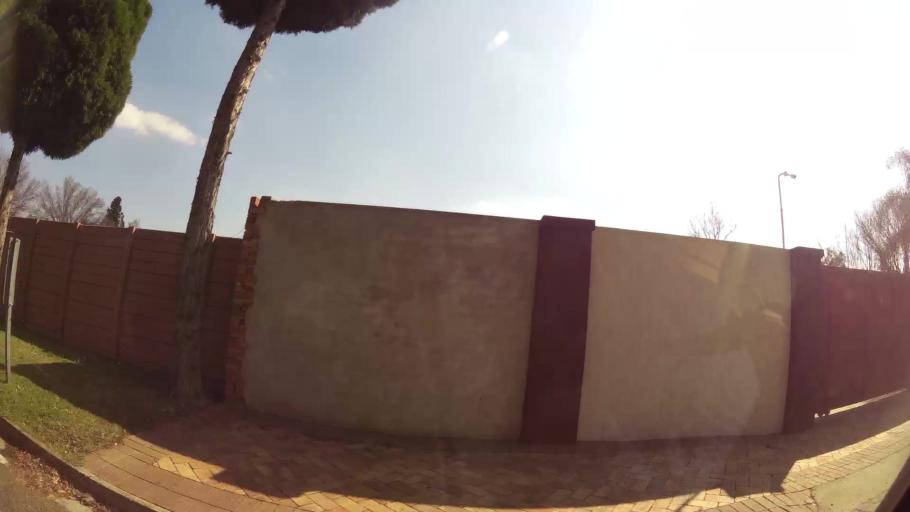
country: ZA
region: Gauteng
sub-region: Ekurhuleni Metropolitan Municipality
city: Benoni
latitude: -26.1867
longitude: 28.2905
